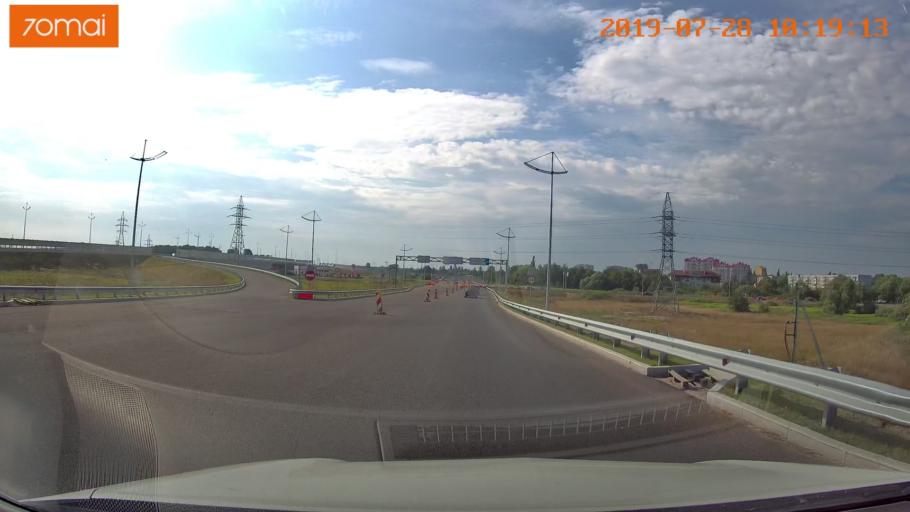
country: RU
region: Kaliningrad
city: Maloye Isakovo
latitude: 54.7499
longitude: 20.5870
